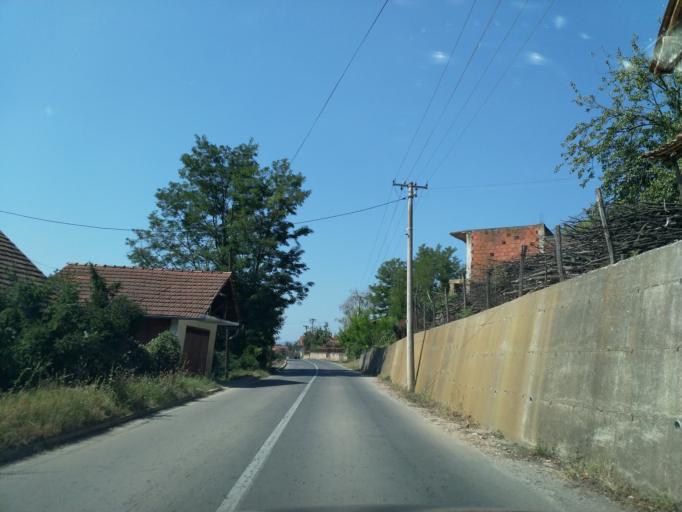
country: RS
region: Central Serbia
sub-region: Rasinski Okrug
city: Krusevac
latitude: 43.6132
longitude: 21.2068
